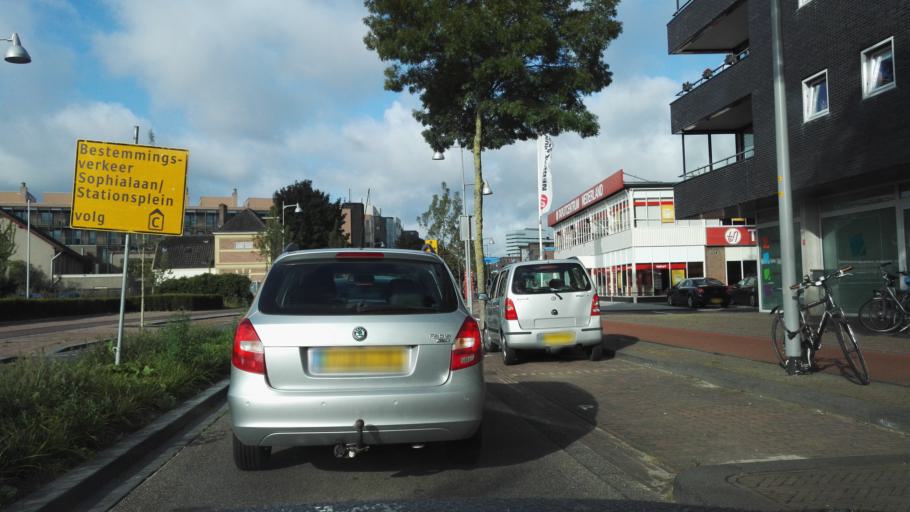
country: NL
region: Gelderland
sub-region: Gemeente Apeldoorn
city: Apeldoorn
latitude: 52.2116
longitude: 5.9721
